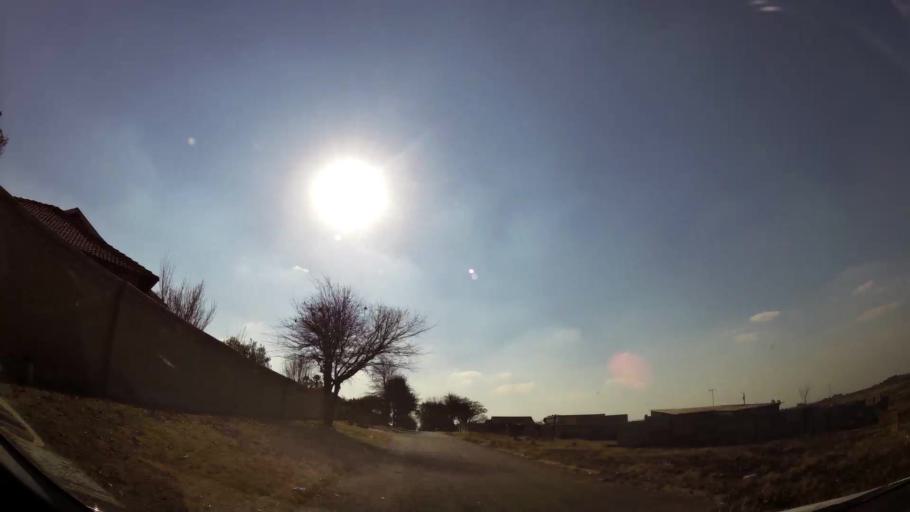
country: ZA
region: Gauteng
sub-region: Ekurhuleni Metropolitan Municipality
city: Brakpan
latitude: -26.2335
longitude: 28.3358
